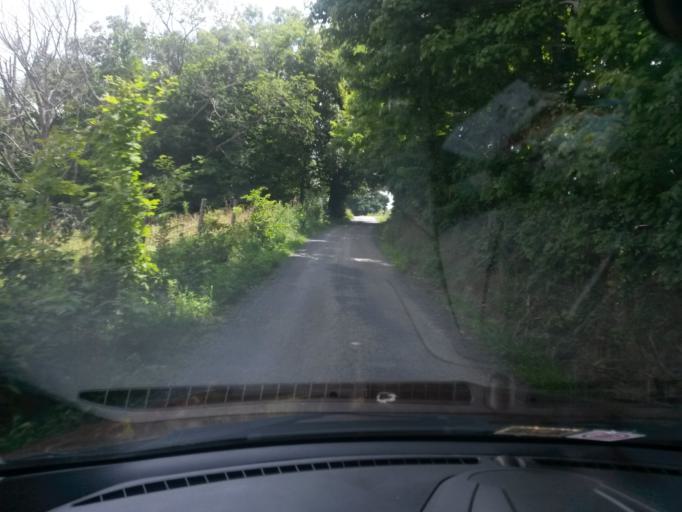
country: US
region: West Virginia
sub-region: Monroe County
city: Union
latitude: 37.5628
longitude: -80.5035
